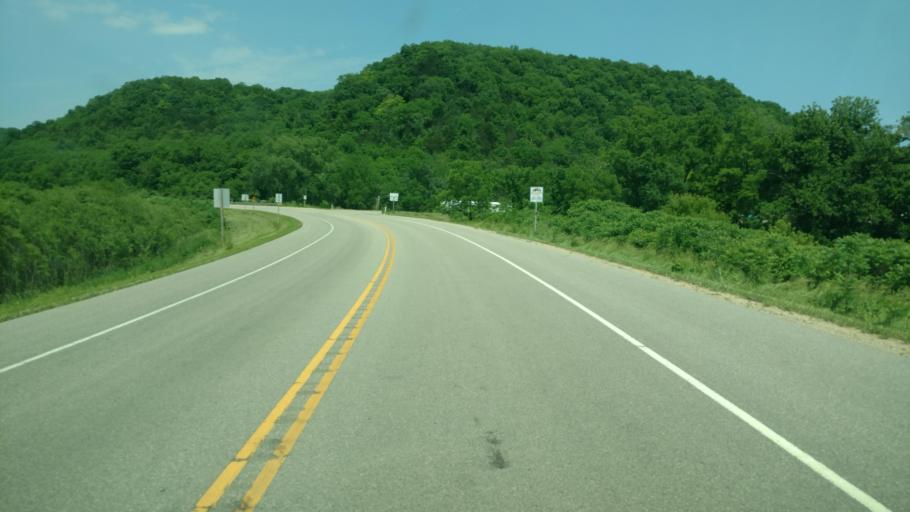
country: US
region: Wisconsin
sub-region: Vernon County
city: Viroqua
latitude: 43.4733
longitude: -90.6923
